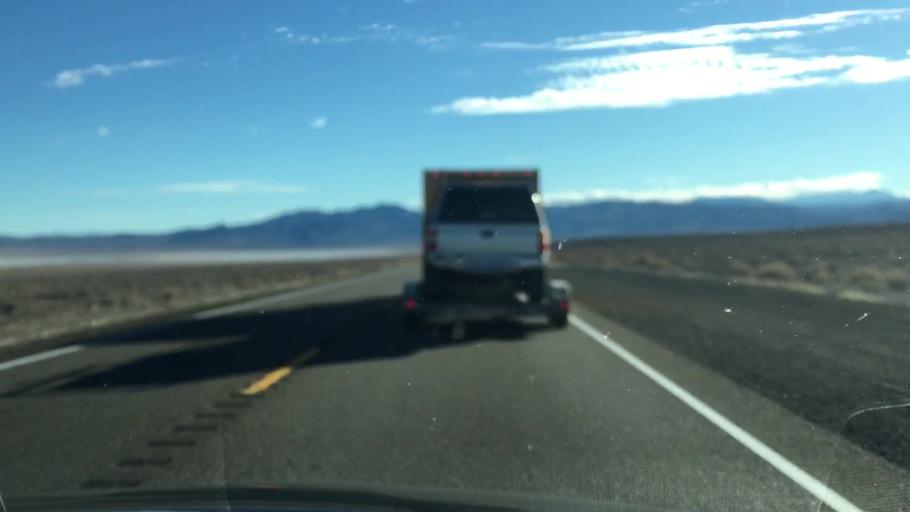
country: US
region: Nevada
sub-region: Mineral County
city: Hawthorne
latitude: 38.3348
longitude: -118.1031
